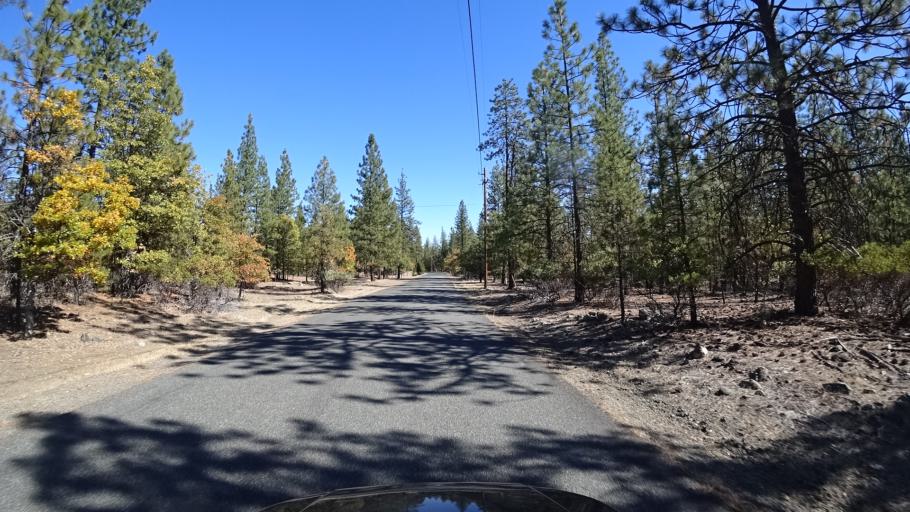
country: US
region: California
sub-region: Siskiyou County
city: Yreka
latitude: 41.5369
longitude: -122.9542
